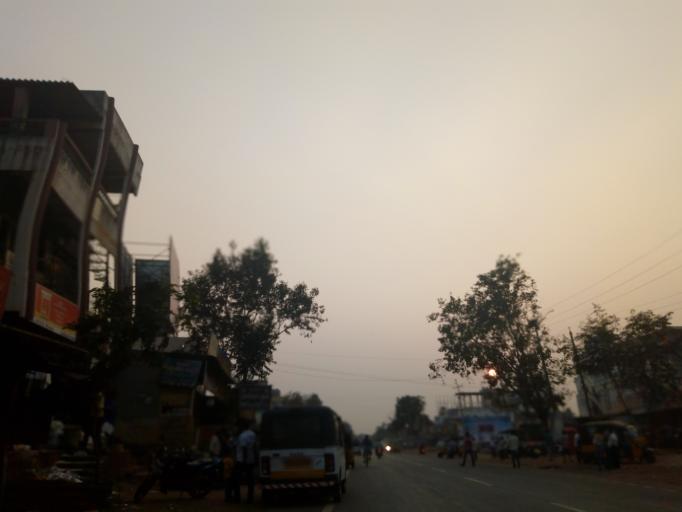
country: IN
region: Andhra Pradesh
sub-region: West Godavari
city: Eluru
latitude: 16.8229
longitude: 81.2626
